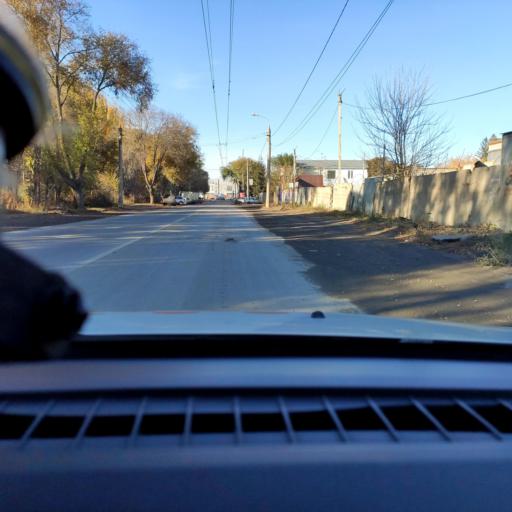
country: RU
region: Samara
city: Samara
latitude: 53.1999
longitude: 50.2669
